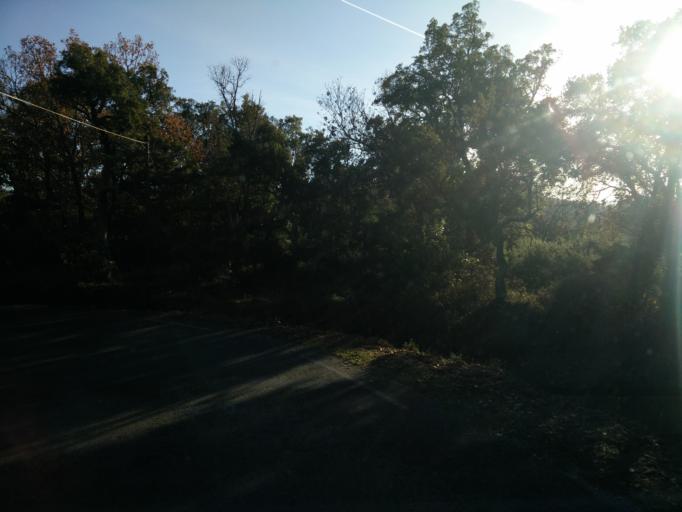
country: FR
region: Provence-Alpes-Cote d'Azur
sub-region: Departement du Var
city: La Garde-Freinet
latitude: 43.3413
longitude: 6.4865
